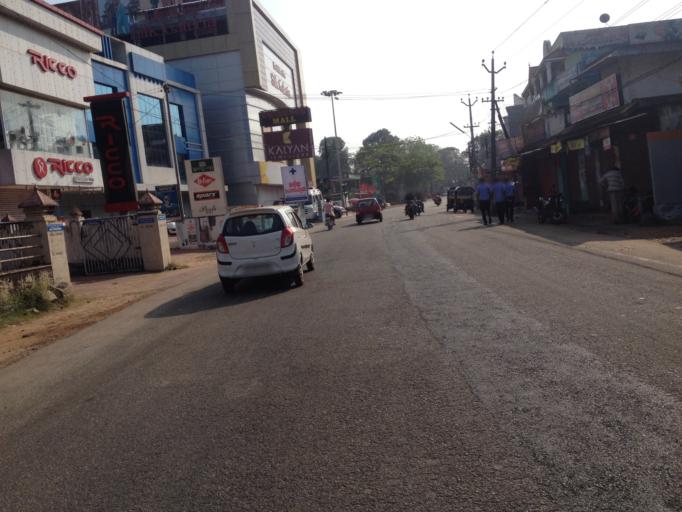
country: IN
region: Kerala
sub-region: Pattanamtitta
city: Adur
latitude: 9.1526
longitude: 76.7414
